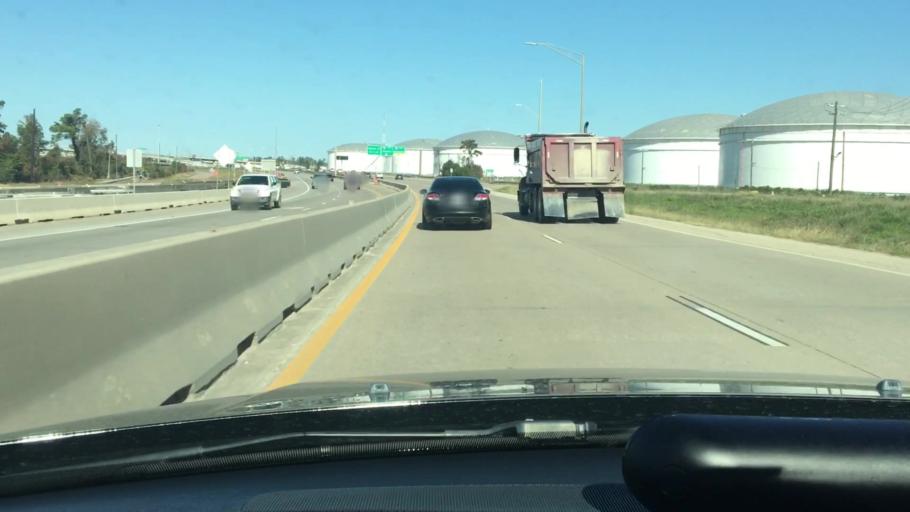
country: US
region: Texas
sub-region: Harris County
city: Cloverleaf
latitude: 29.7579
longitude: -95.1460
